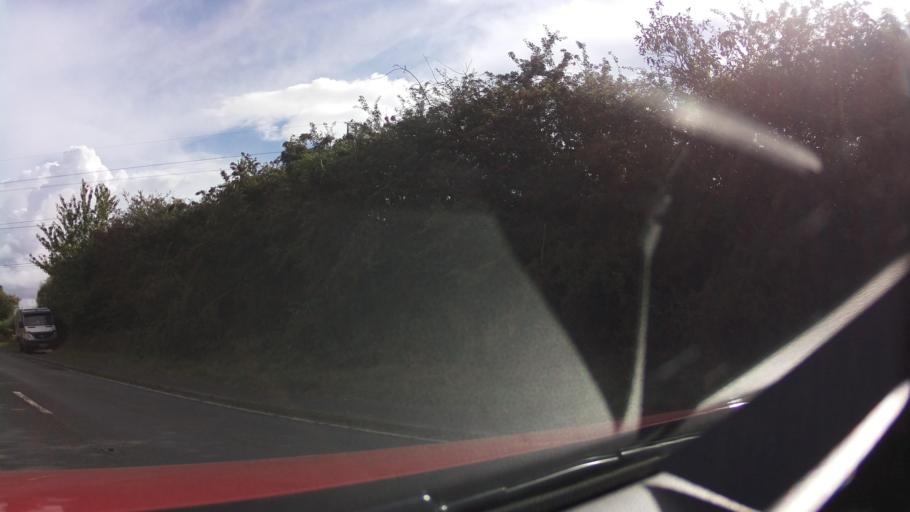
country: GB
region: England
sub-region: Telford and Wrekin
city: Madeley
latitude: 52.6073
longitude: -2.4080
